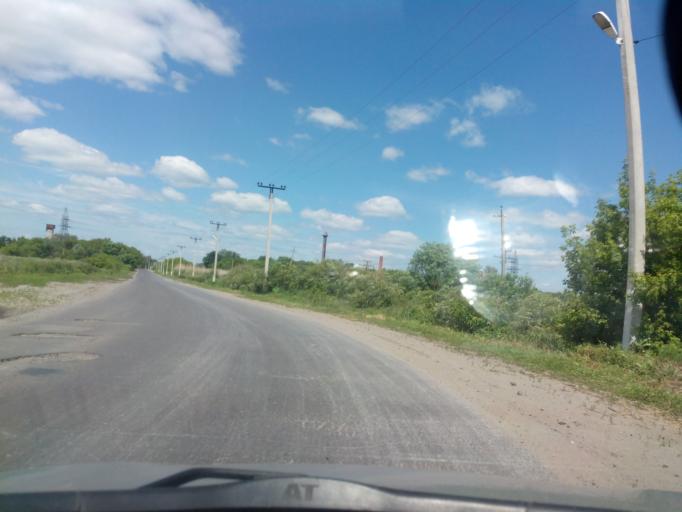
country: RU
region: Tambov
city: Zherdevka
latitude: 51.8053
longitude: 41.5051
